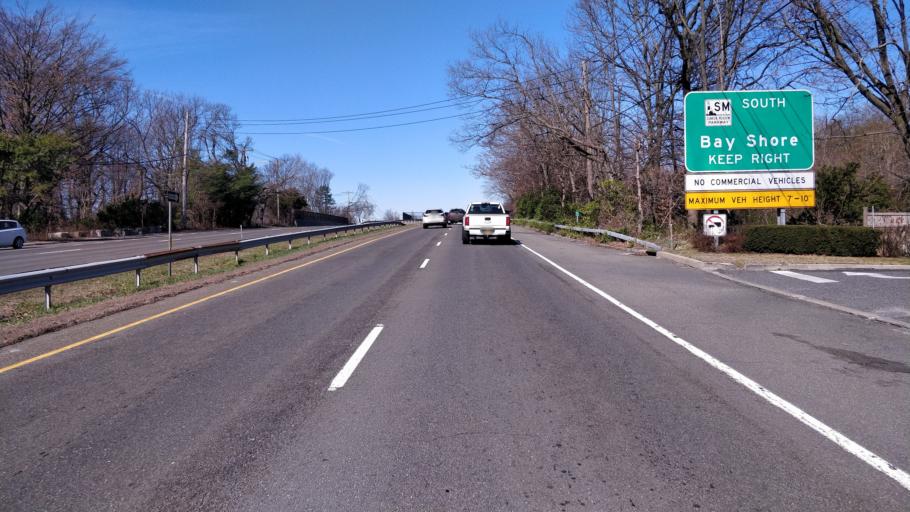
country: US
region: New York
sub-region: Suffolk County
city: Commack
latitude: 40.8392
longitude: -73.2796
